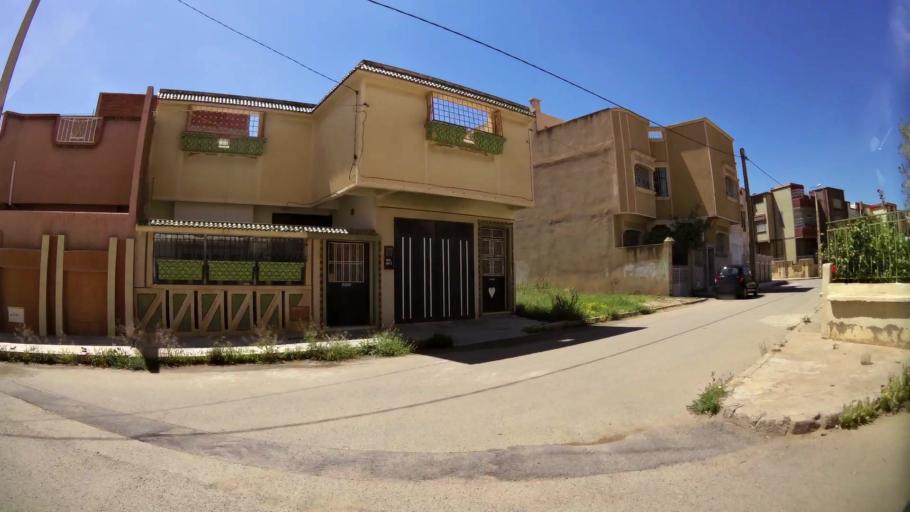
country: MA
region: Oriental
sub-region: Oujda-Angad
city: Oujda
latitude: 34.6632
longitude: -1.9326
